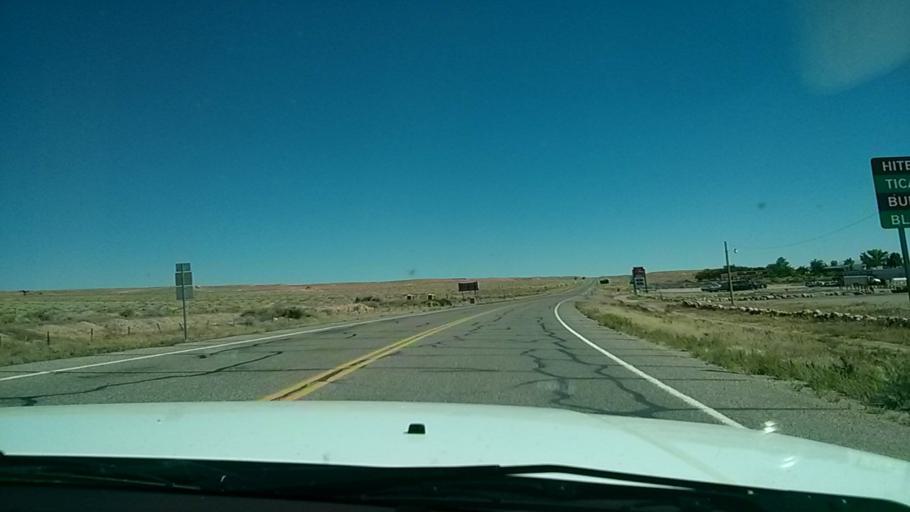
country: US
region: Utah
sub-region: Emery County
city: Ferron
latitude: 38.3725
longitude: -110.7041
